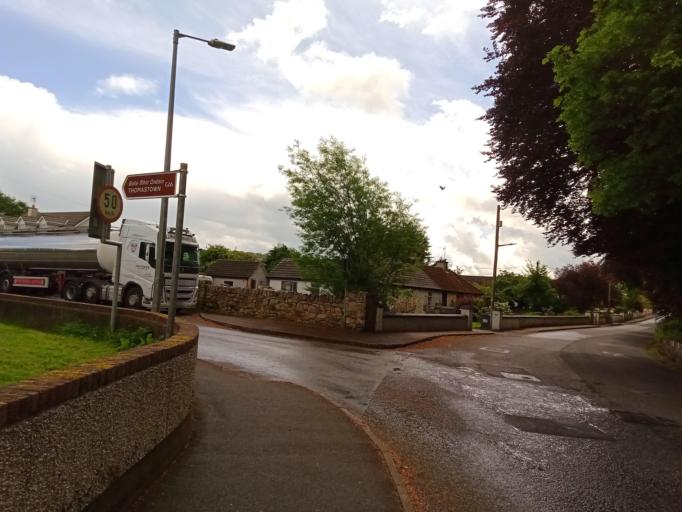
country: IE
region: Leinster
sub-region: Kilkenny
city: Thomastown
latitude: 52.5213
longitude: -7.1356
